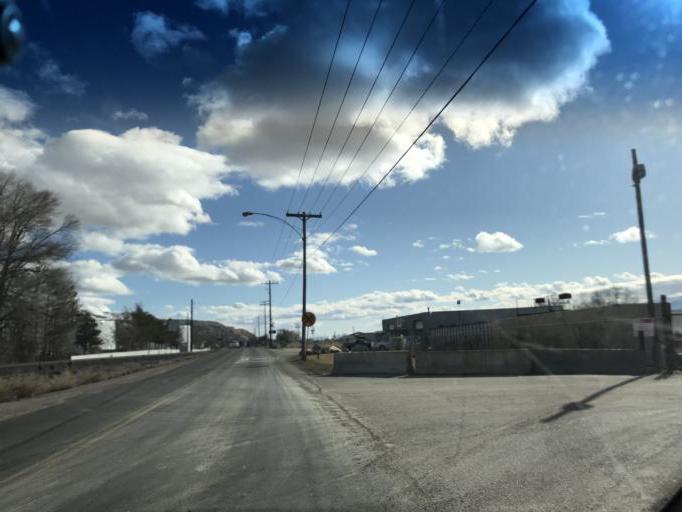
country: US
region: Utah
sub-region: Davis County
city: Woods Cross
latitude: 40.8702
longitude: -111.9119
